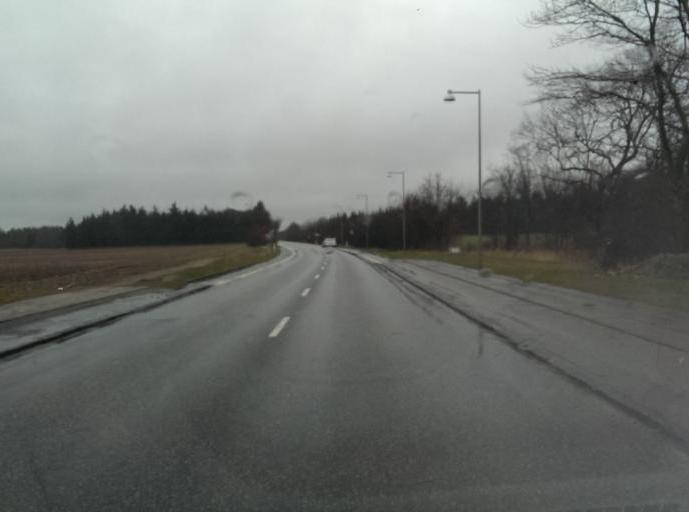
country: DK
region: Central Jutland
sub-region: Ringkobing-Skjern Kommune
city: Tarm
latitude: 55.8027
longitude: 8.4924
